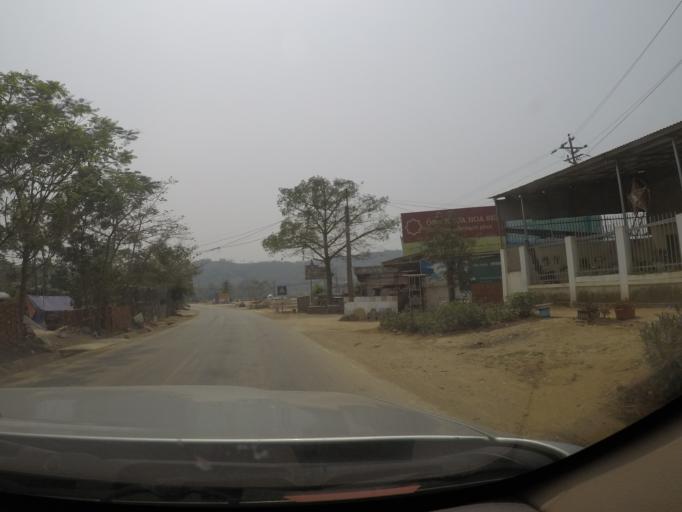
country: VN
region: Thanh Hoa
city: Thi Tran Thuong Xuan
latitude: 19.9661
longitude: 105.3978
